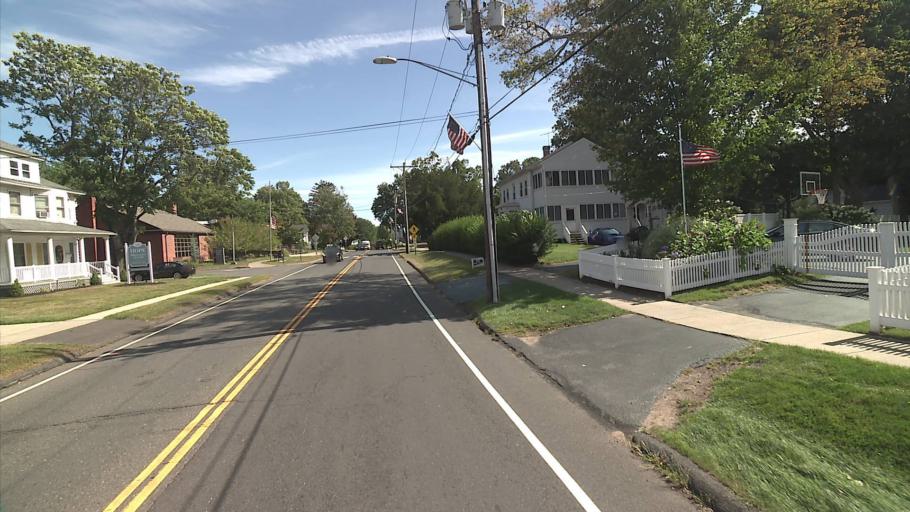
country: US
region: Connecticut
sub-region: New Haven County
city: Cheshire Village
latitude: 41.5023
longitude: -72.9028
